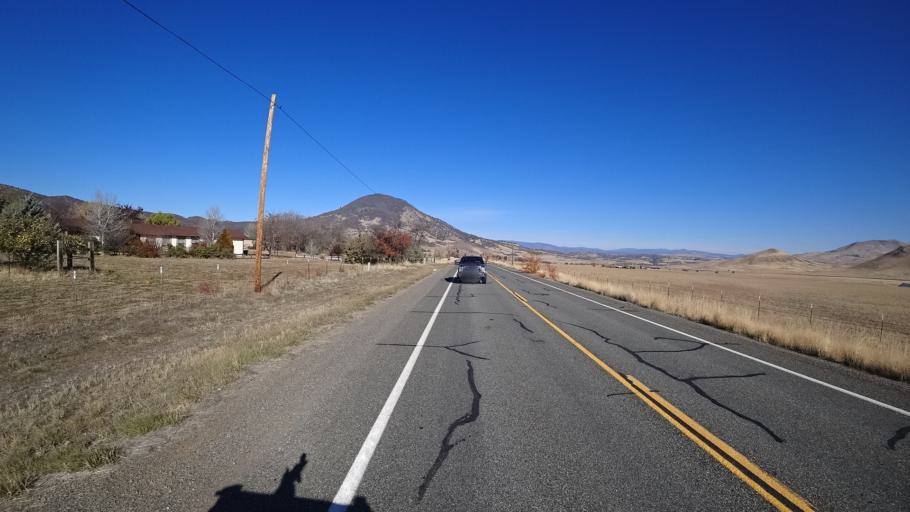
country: US
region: California
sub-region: Siskiyou County
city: Montague
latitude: 41.8106
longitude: -122.4984
